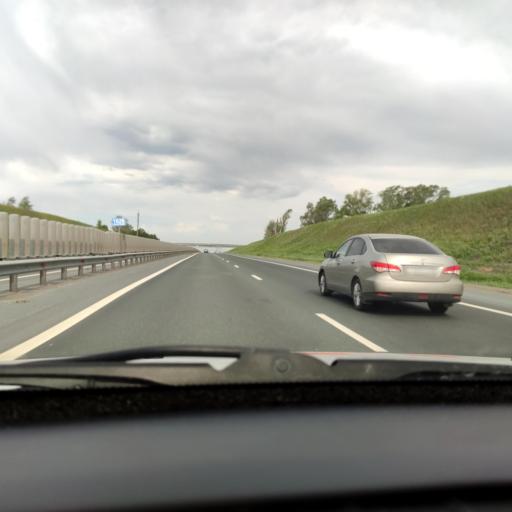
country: RU
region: Samara
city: Mirnyy
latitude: 53.4483
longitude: 50.2552
